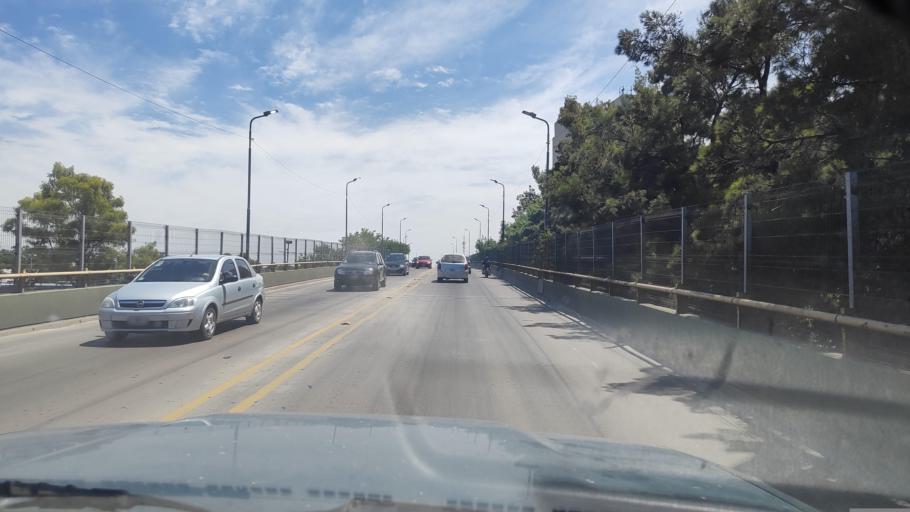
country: AR
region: Buenos Aires
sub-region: Partido de Moron
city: Moron
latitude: -34.6500
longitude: -58.6290
